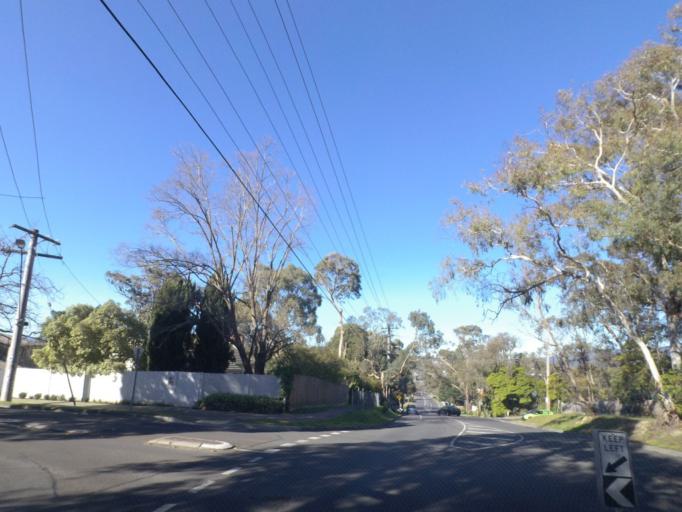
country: AU
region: Victoria
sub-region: Maroondah
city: Croydon North
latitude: -37.7696
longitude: 145.2869
